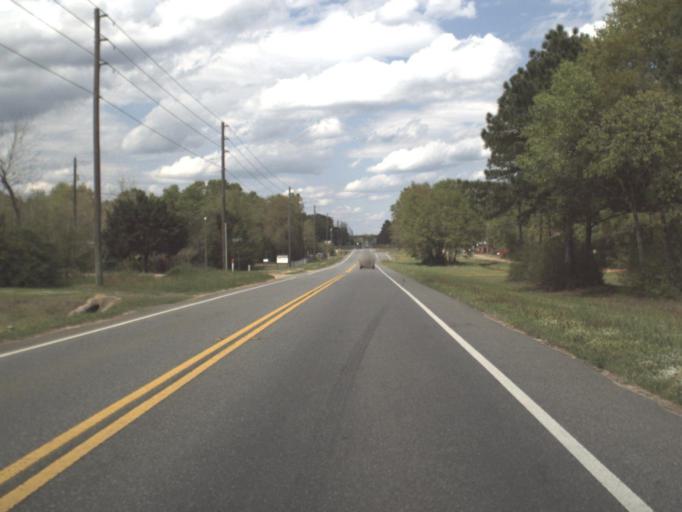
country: US
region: Florida
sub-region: Okaloosa County
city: Crestview
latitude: 30.8302
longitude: -86.5340
